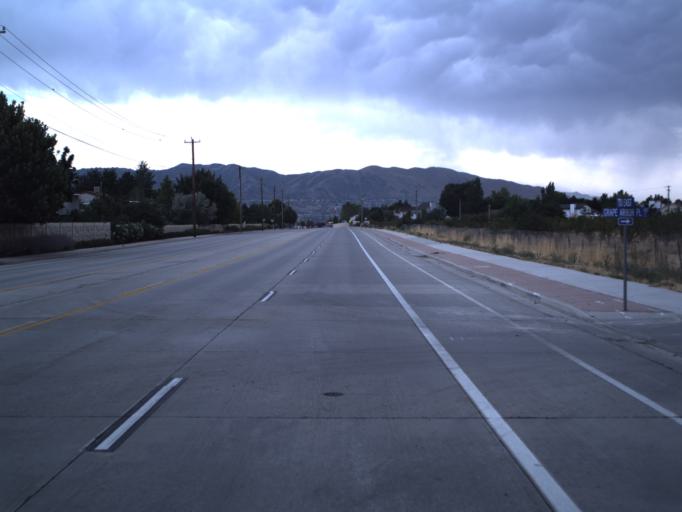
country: US
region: Utah
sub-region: Salt Lake County
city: White City
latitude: 40.5498
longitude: -111.8724
